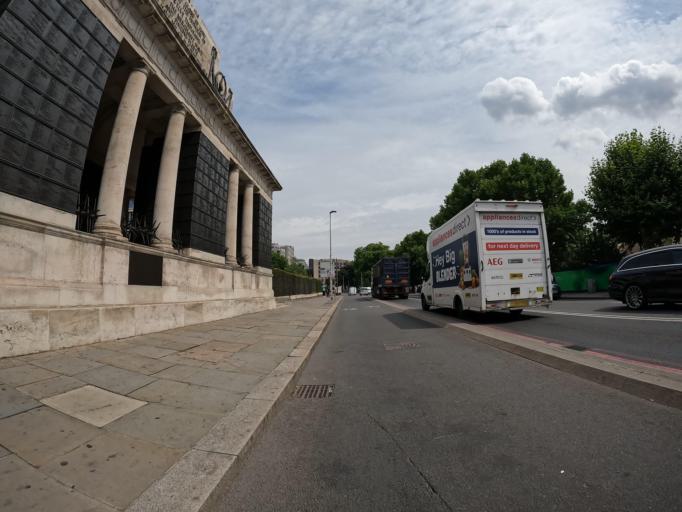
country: GB
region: England
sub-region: Surrey
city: Woking
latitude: 51.2919
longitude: -0.5547
